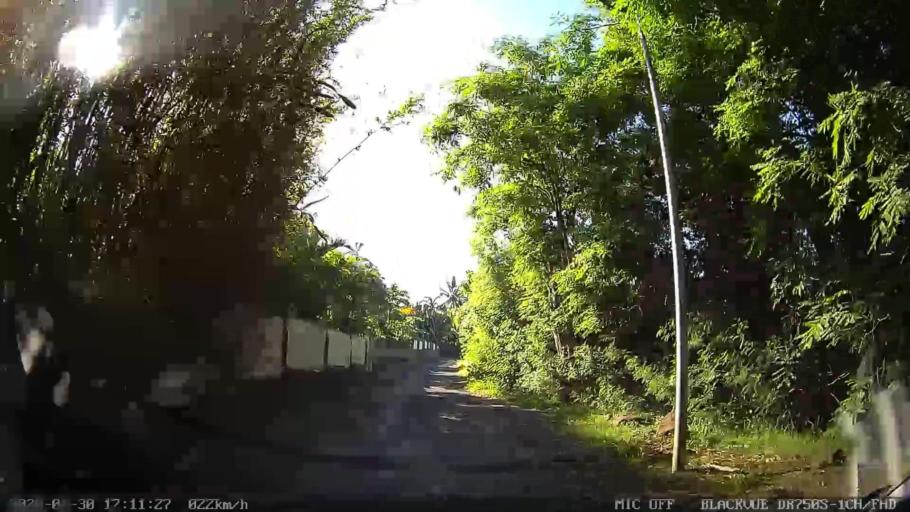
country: RE
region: Reunion
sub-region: Reunion
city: Sainte-Marie
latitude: -20.9143
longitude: 55.5123
